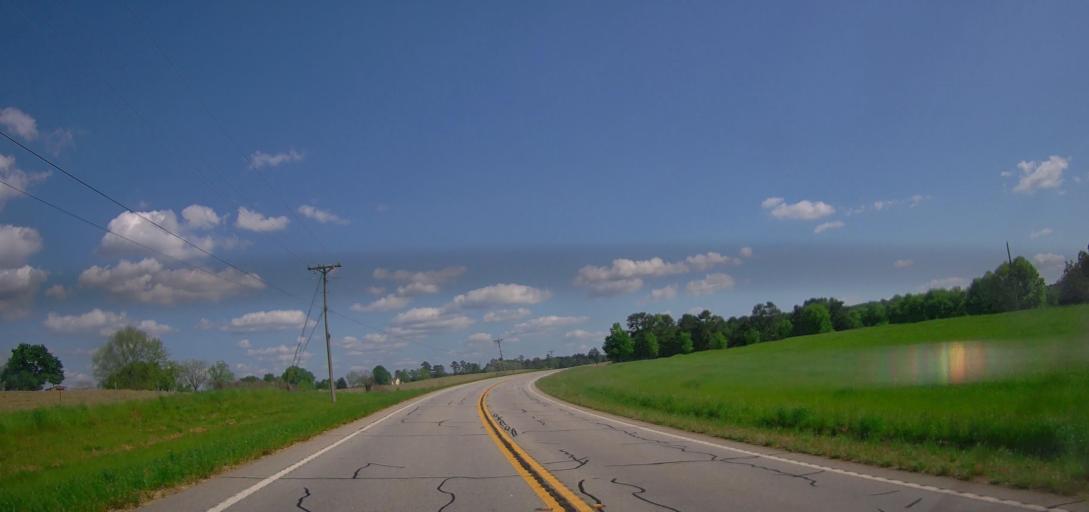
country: US
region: Georgia
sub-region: Greene County
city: Greensboro
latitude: 33.6117
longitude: -83.3126
